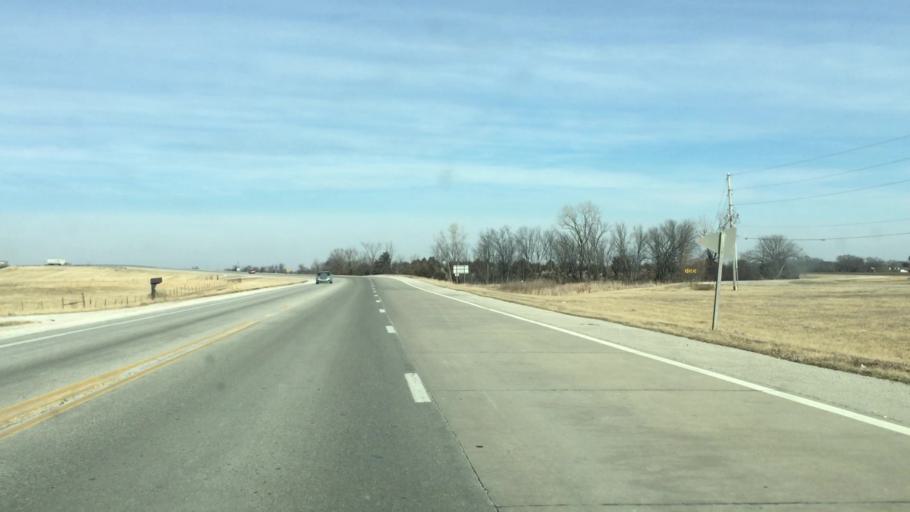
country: US
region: Kansas
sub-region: Labette County
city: Parsons
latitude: 37.3770
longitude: -95.2584
